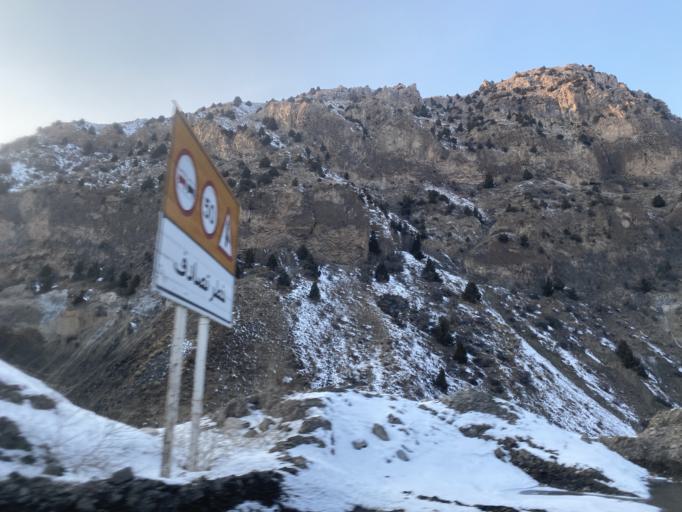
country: IR
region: Tehran
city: Damavand
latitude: 35.8570
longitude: 52.0890
